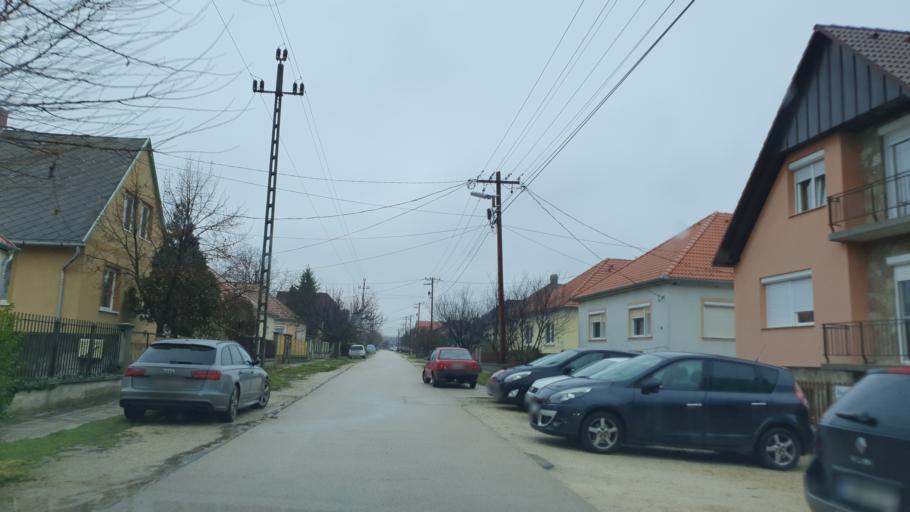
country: HU
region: Veszprem
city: Veszprem
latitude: 47.1412
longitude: 17.9431
